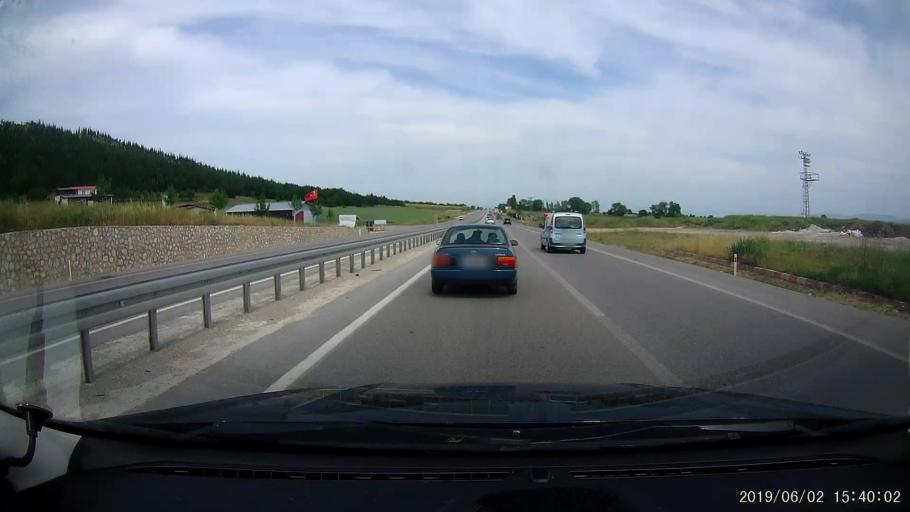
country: TR
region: Amasya
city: Gumushacikoy
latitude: 40.8664
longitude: 35.2715
